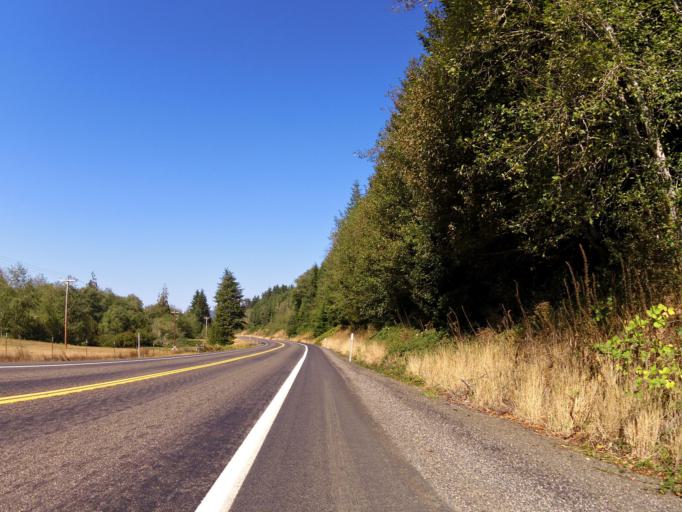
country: US
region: Oregon
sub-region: Tillamook County
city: Tillamook
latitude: 45.3252
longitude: -123.8499
